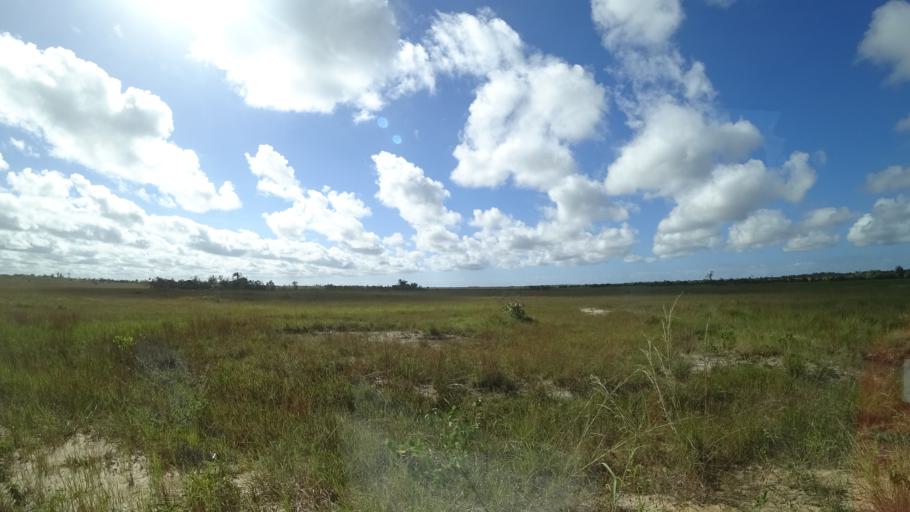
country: MZ
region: Sofala
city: Beira
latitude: -19.6265
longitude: 35.0603
